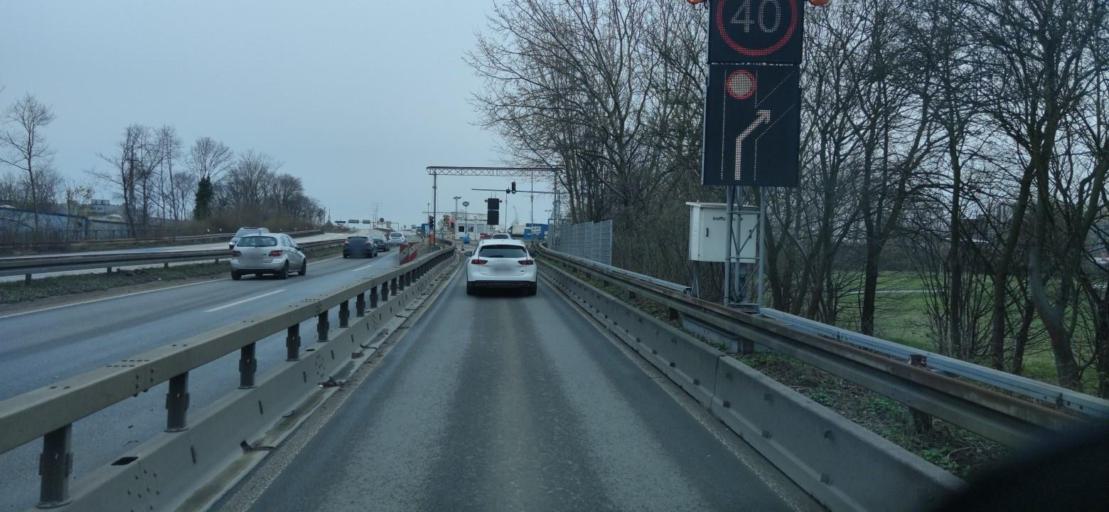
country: DE
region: North Rhine-Westphalia
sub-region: Regierungsbezirk Dusseldorf
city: Duisburg
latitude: 51.4377
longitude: 6.7469
